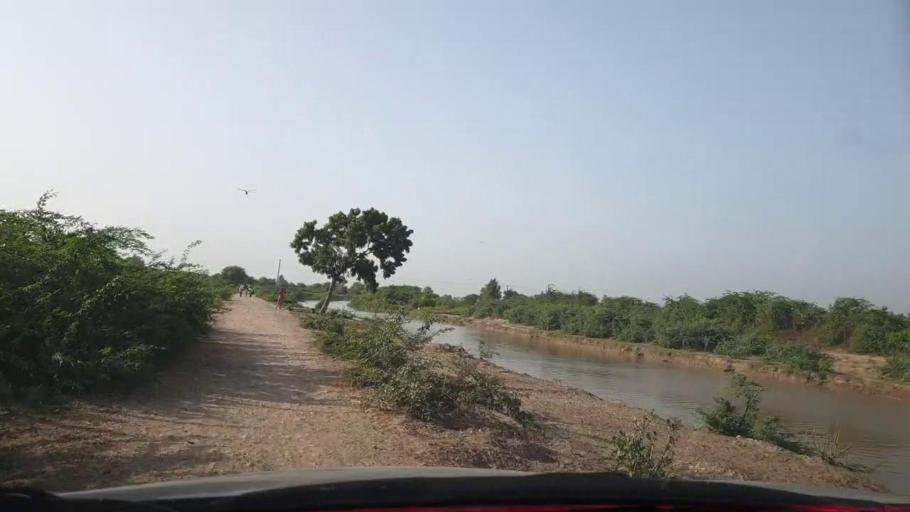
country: PK
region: Sindh
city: Talhar
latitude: 24.8943
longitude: 68.8218
